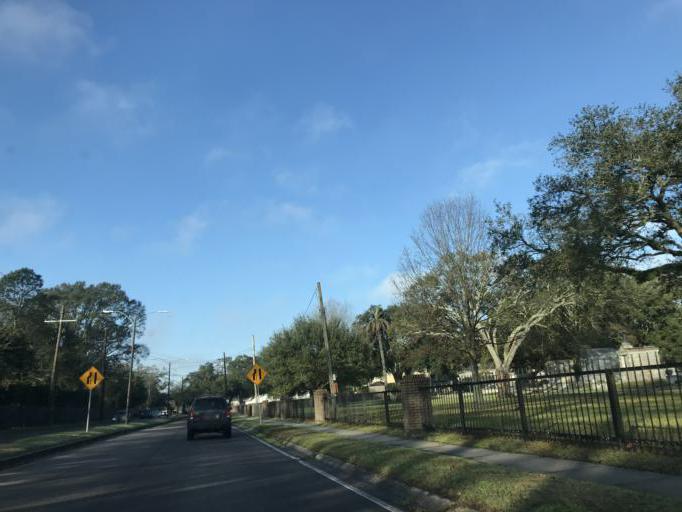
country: US
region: Louisiana
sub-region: Jefferson Parish
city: Metairie
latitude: 29.9800
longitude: -90.1206
